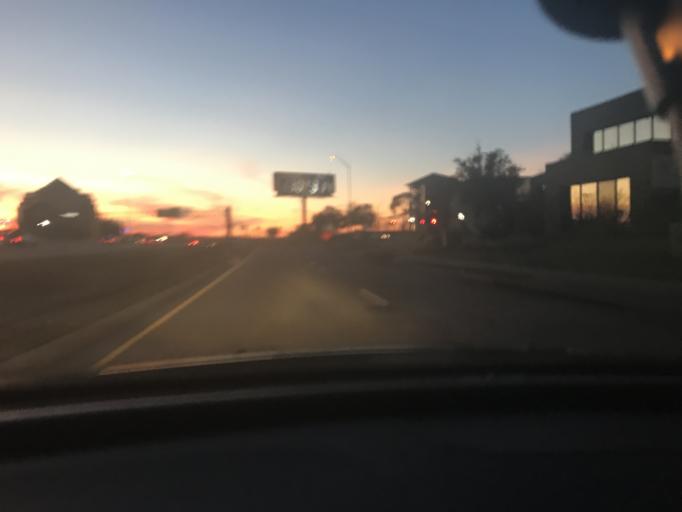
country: US
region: Texas
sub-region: Tarrant County
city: Arlington
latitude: 32.7602
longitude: -97.1090
